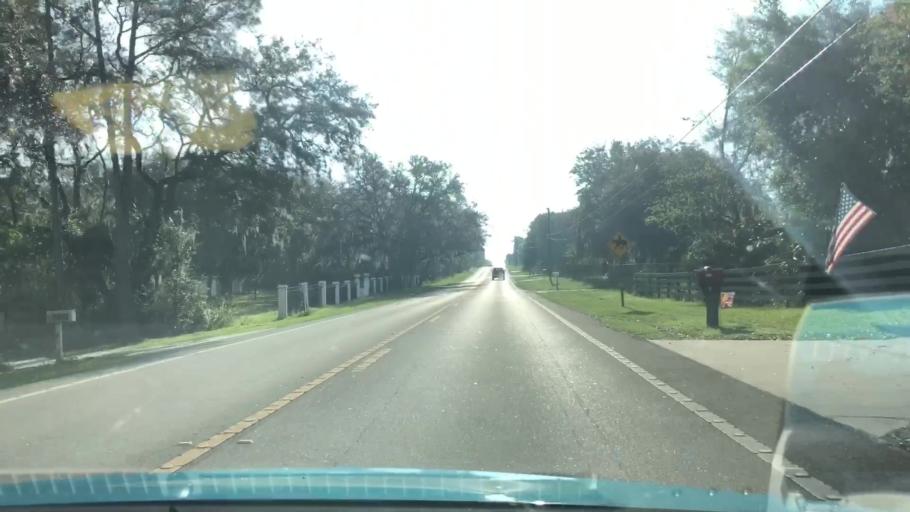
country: US
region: Florida
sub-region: Volusia County
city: Deltona
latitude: 28.8653
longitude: -81.2167
